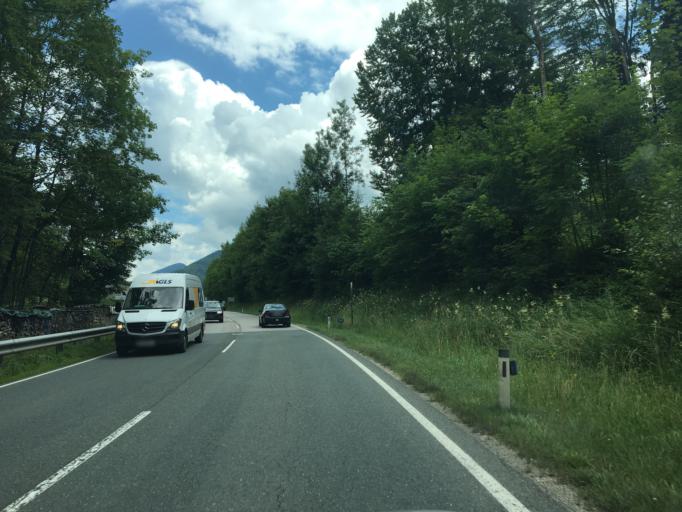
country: AT
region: Salzburg
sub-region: Politischer Bezirk Salzburg-Umgebung
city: Plainfeld
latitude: 47.8270
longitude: 13.1951
